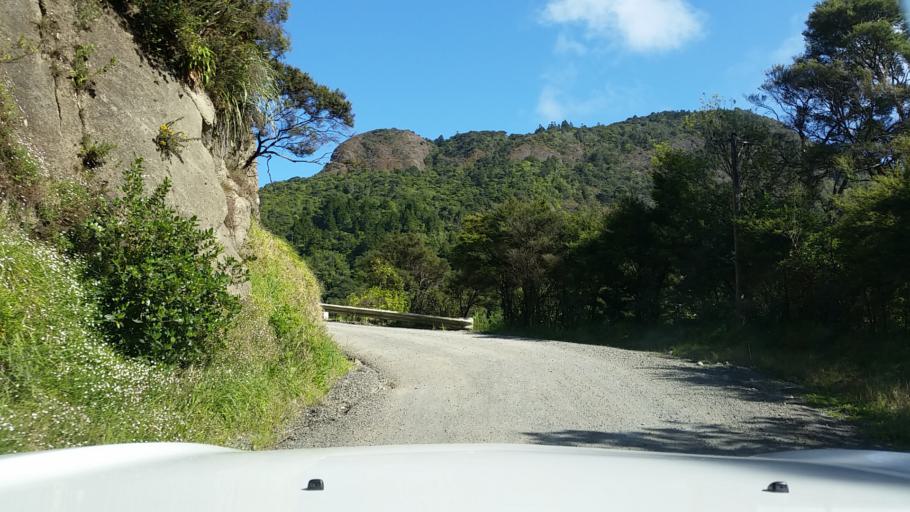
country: NZ
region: Auckland
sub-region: Auckland
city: Titirangi
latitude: -37.0206
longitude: 174.5445
